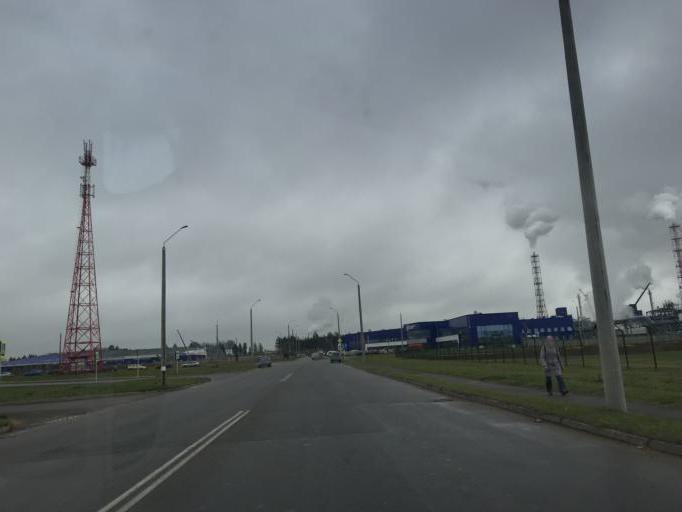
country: BY
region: Mogilev
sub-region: Mahilyowski Rayon
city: Veyno
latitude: 53.8288
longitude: 30.3504
